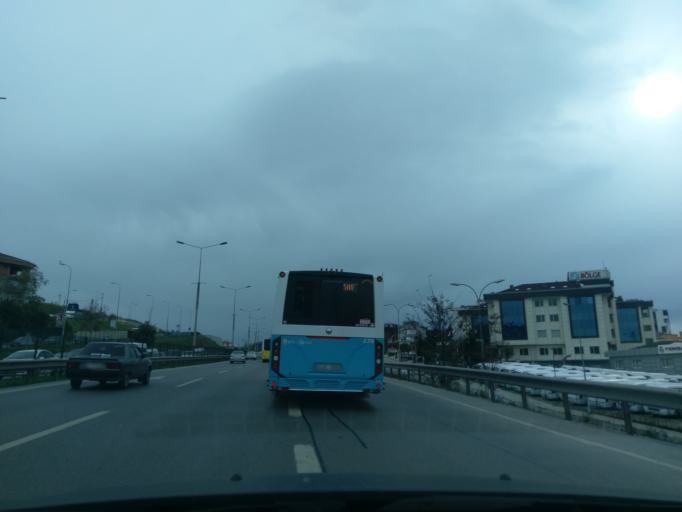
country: TR
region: Istanbul
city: Pendik
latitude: 40.8840
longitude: 29.2450
